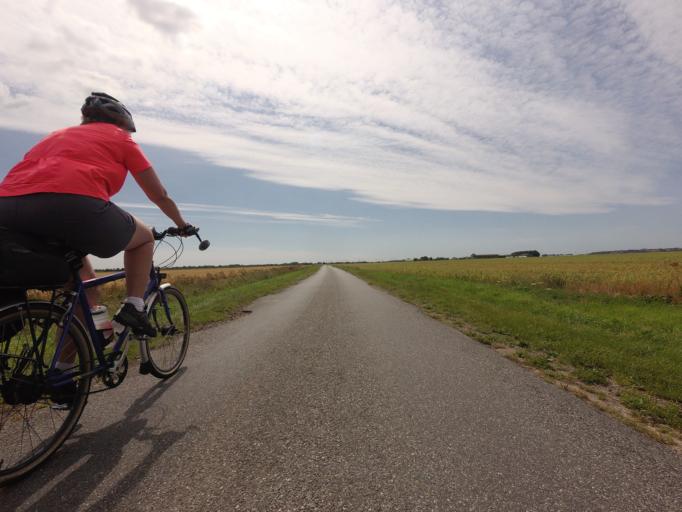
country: GB
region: England
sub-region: Kent
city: Stone
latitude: 51.0220
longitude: 0.7963
